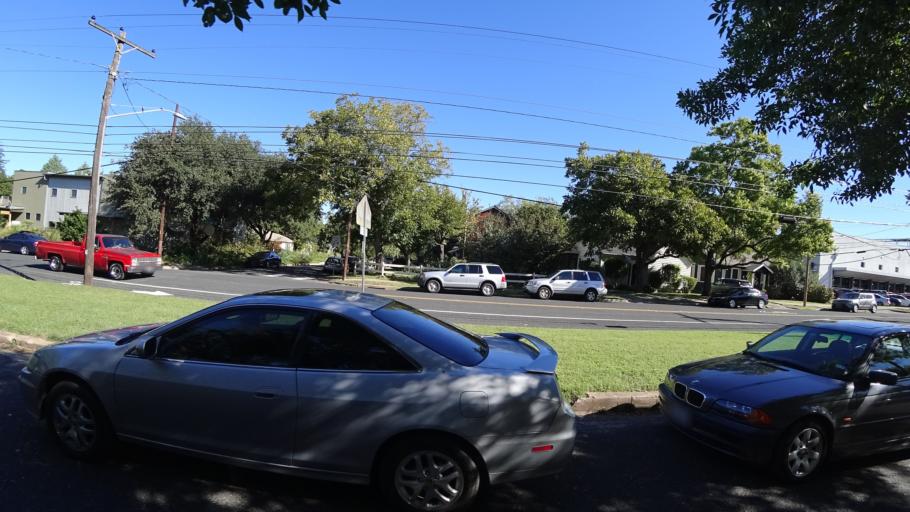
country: US
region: Texas
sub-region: Travis County
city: Austin
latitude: 30.2423
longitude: -97.7537
